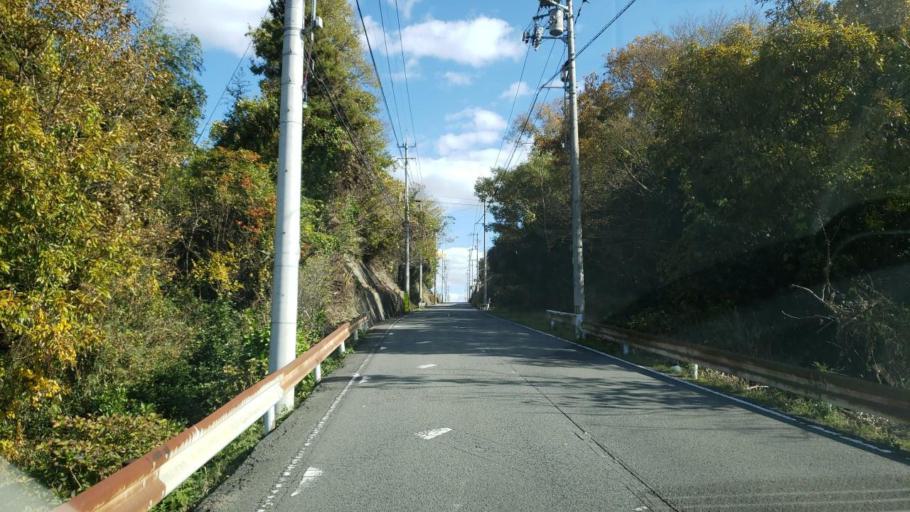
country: JP
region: Tokushima
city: Wakimachi
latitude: 34.0817
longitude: 134.2129
